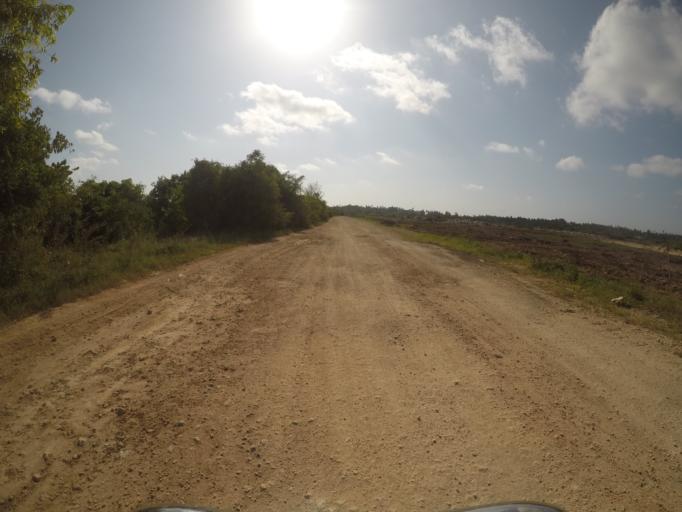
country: TZ
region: Zanzibar Central/South
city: Koani
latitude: -6.2180
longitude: 39.3314
